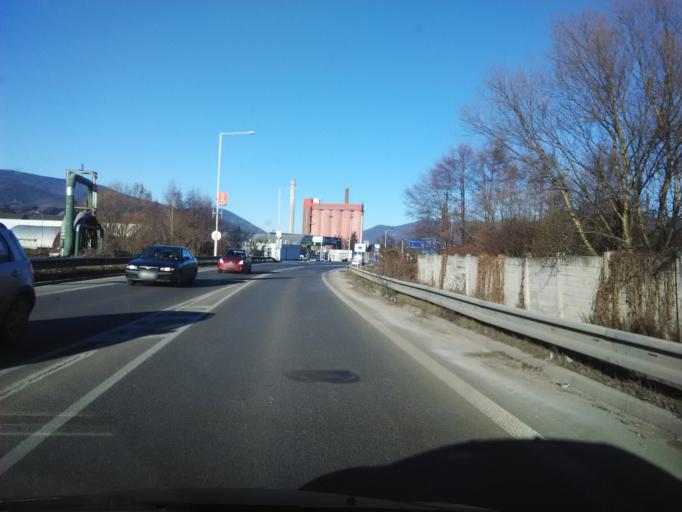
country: SK
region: Zilinsky
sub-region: Okres Martin
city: Martin
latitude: 49.0605
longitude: 18.9093
